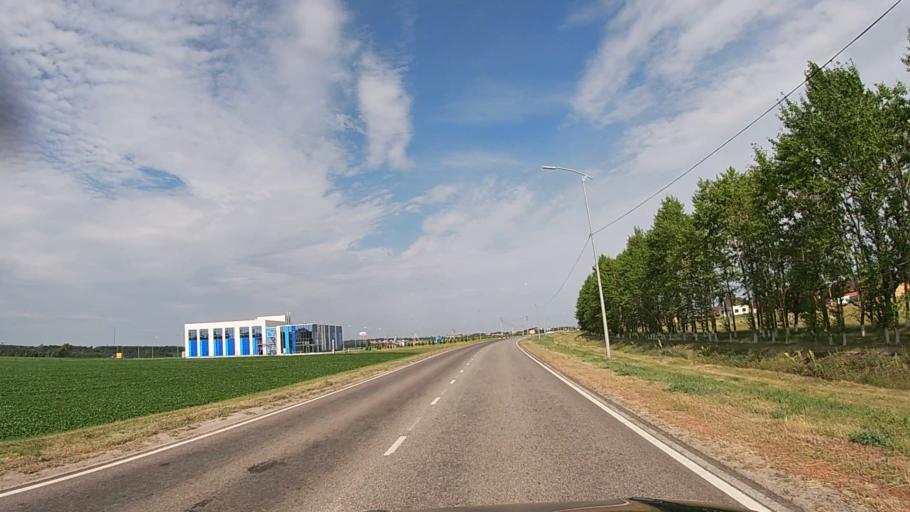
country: RU
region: Belgorod
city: Krasnaya Yaruga
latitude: 50.7963
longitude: 35.6941
